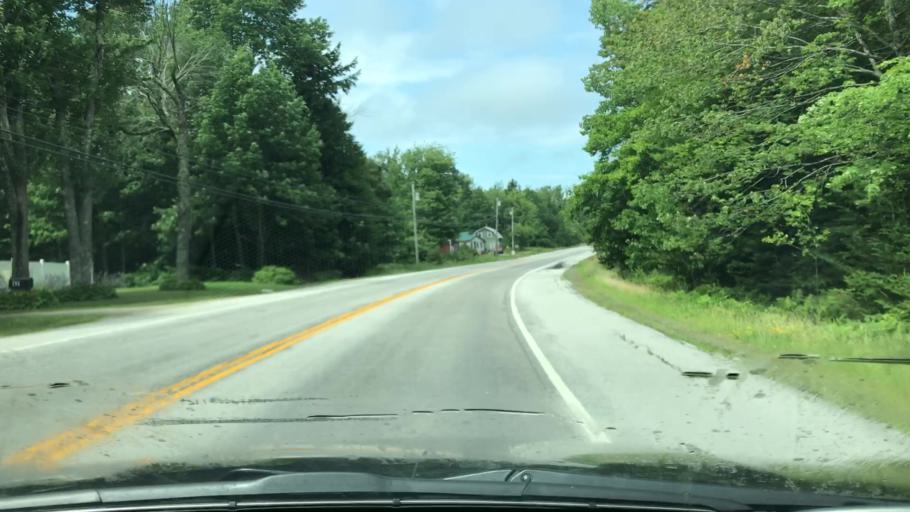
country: US
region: Maine
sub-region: Waldo County
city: Northport
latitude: 44.3446
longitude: -68.9697
